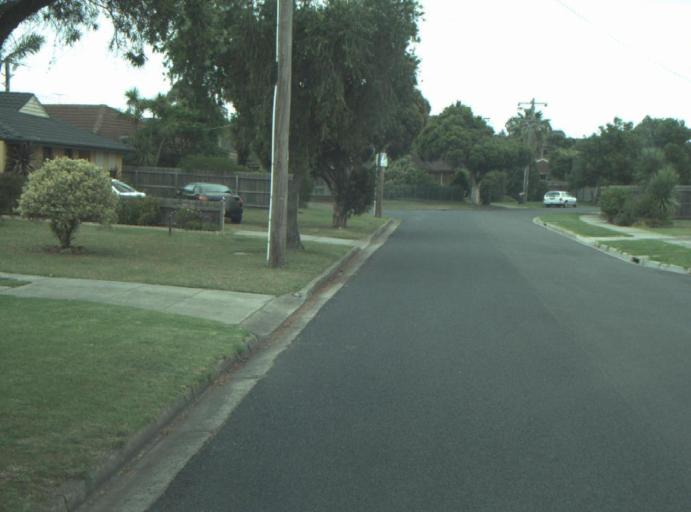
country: AU
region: Victoria
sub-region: Greater Geelong
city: Wandana Heights
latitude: -38.2022
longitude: 144.3281
